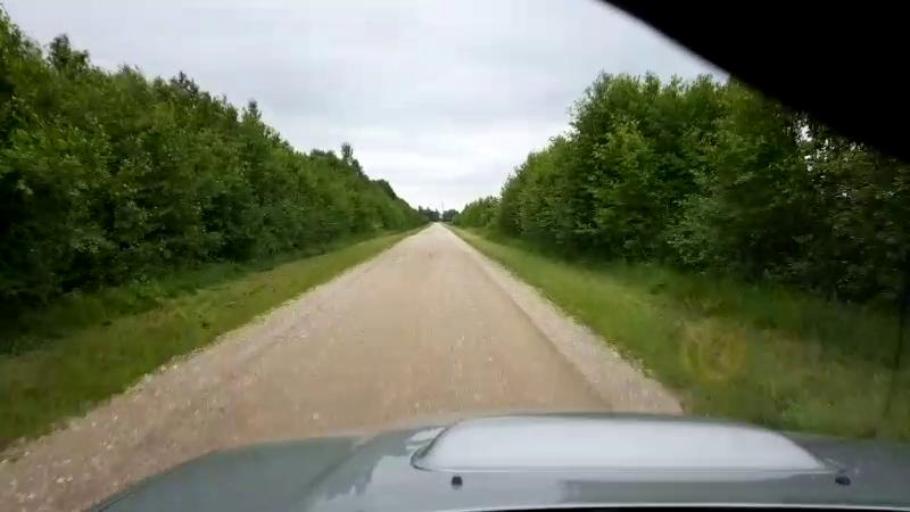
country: EE
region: Paernumaa
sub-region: Halinga vald
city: Parnu-Jaagupi
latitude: 58.5455
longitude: 24.5596
